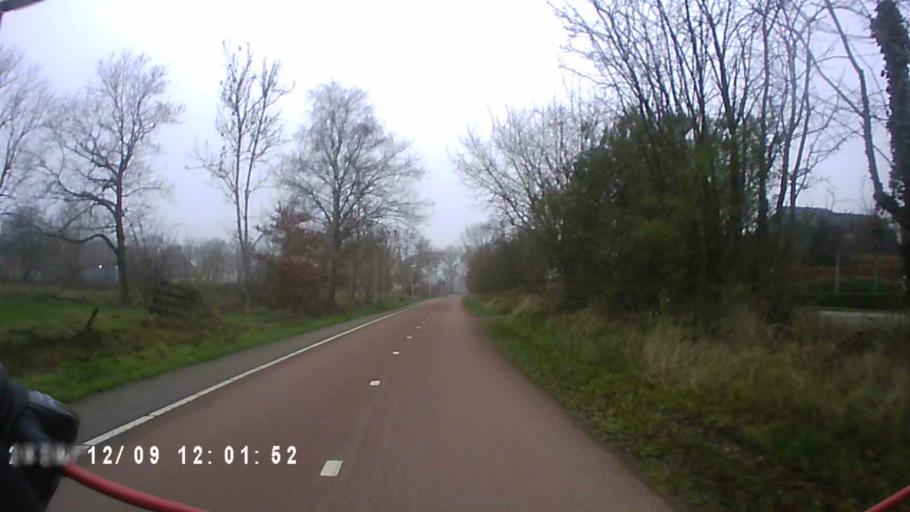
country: NL
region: Groningen
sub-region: Gemeente Haren
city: Haren
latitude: 53.1858
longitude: 6.6000
